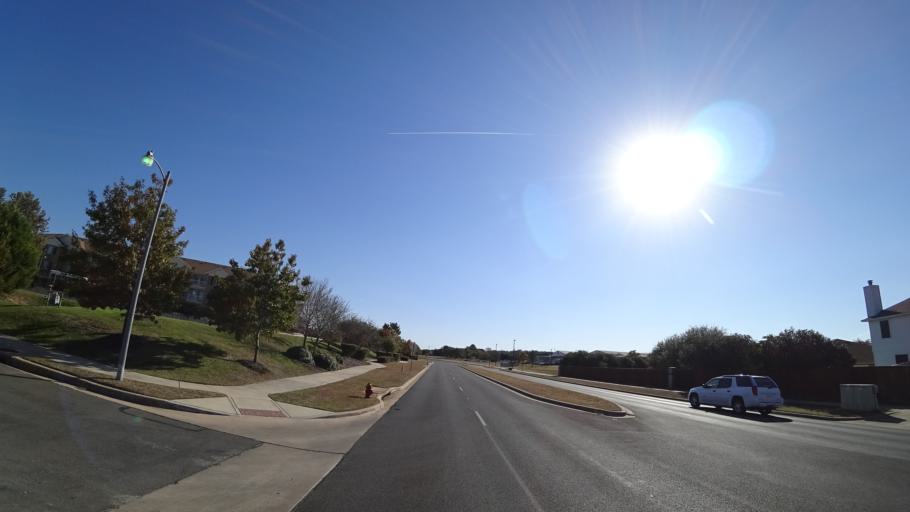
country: US
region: Texas
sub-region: Williamson County
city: Cedar Park
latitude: 30.5232
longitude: -97.8540
